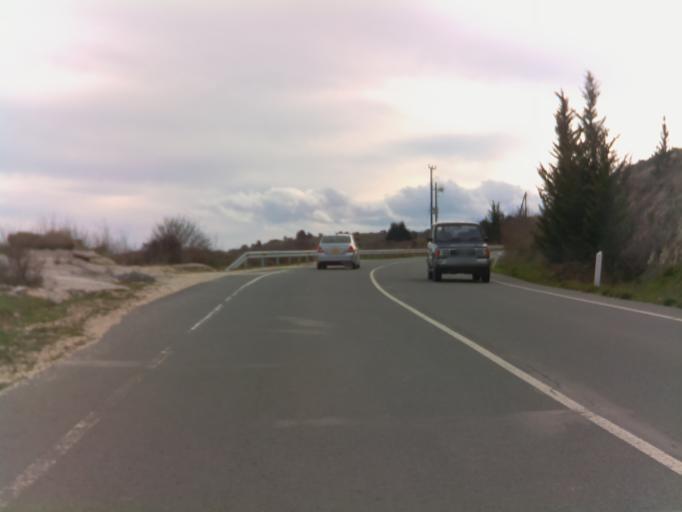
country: CY
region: Pafos
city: Pegeia
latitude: 34.9567
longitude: 32.4119
